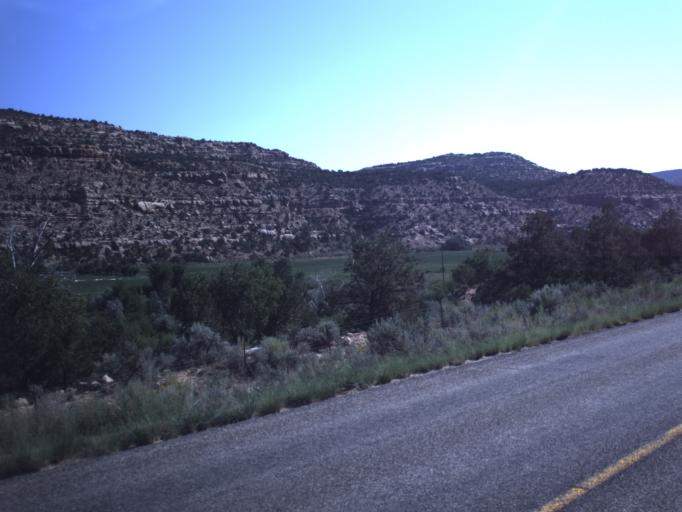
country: US
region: Utah
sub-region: Duchesne County
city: Duchesne
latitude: 40.2987
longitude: -110.5300
